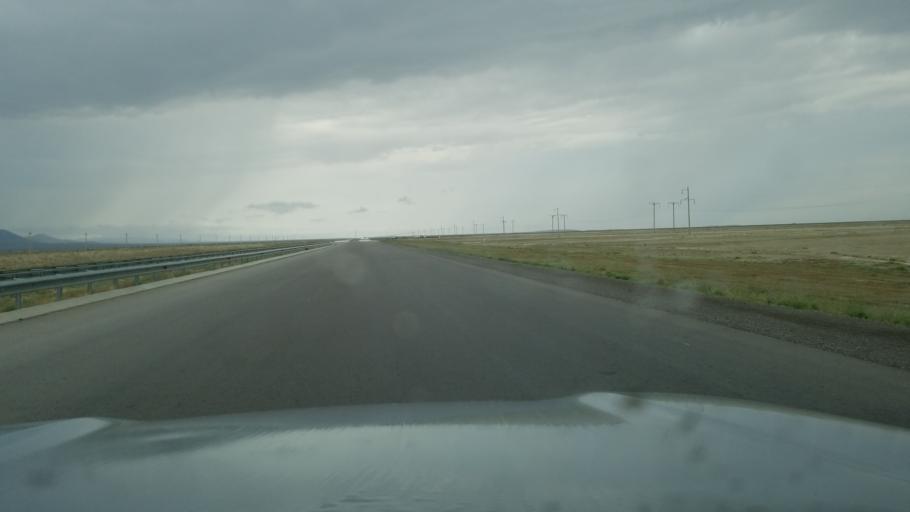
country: TM
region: Balkan
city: Serdar
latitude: 39.0410
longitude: 56.1540
